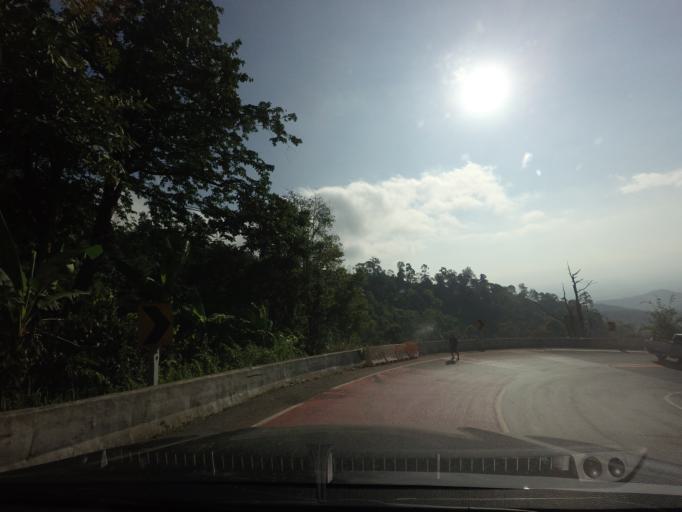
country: TH
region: Phetchabun
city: Lom Kao
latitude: 16.8877
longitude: 101.1212
